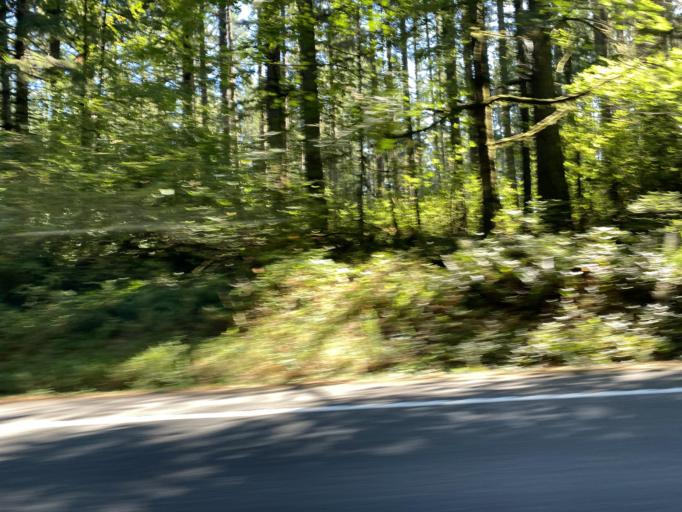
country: US
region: Washington
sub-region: Thurston County
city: Rainier
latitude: 46.9273
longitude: -122.7518
